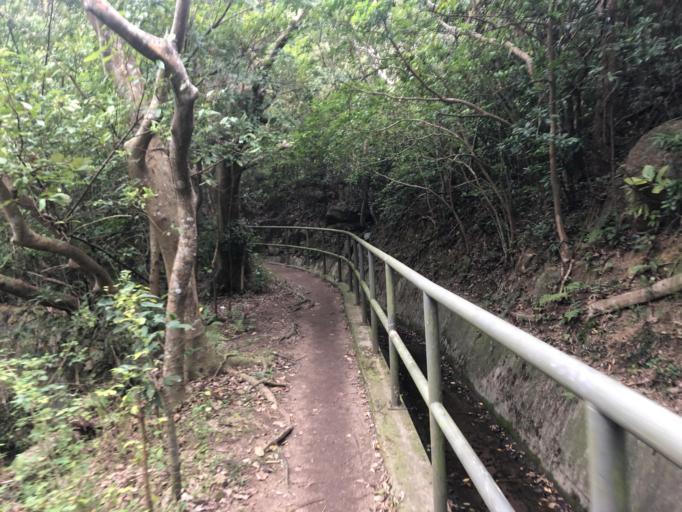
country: HK
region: Wanchai
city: Wan Chai
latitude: 22.2734
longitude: 114.2283
